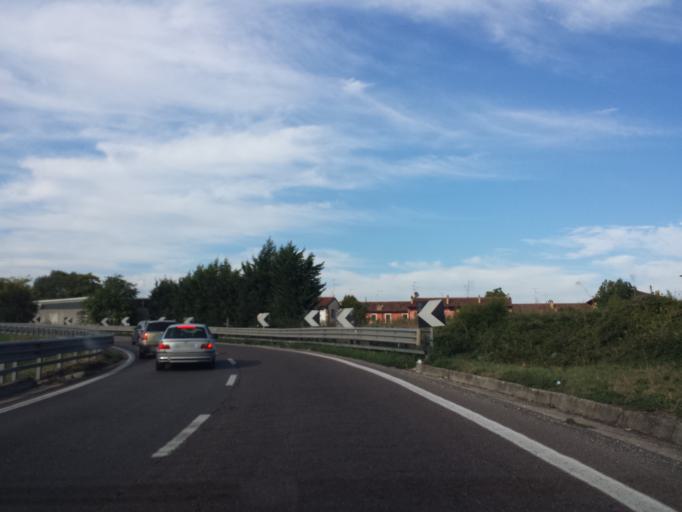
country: IT
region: Veneto
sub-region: Provincia di Verona
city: San Giovanni Lupatoto
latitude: 45.4030
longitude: 11.0106
